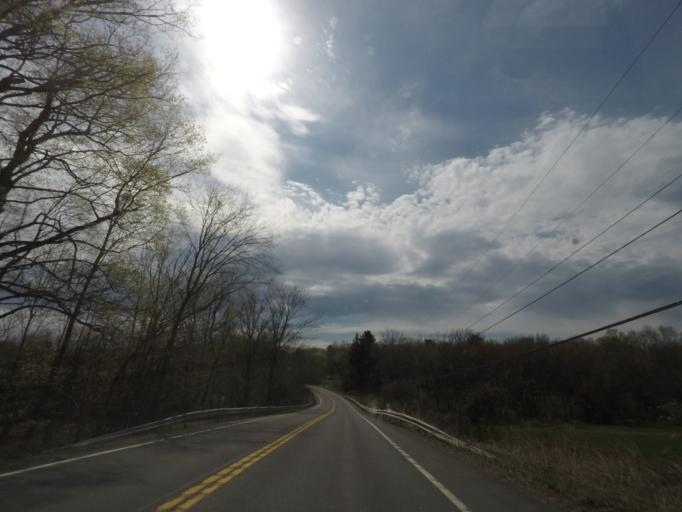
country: US
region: New York
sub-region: Columbia County
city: Stottville
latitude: 42.2892
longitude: -73.6950
